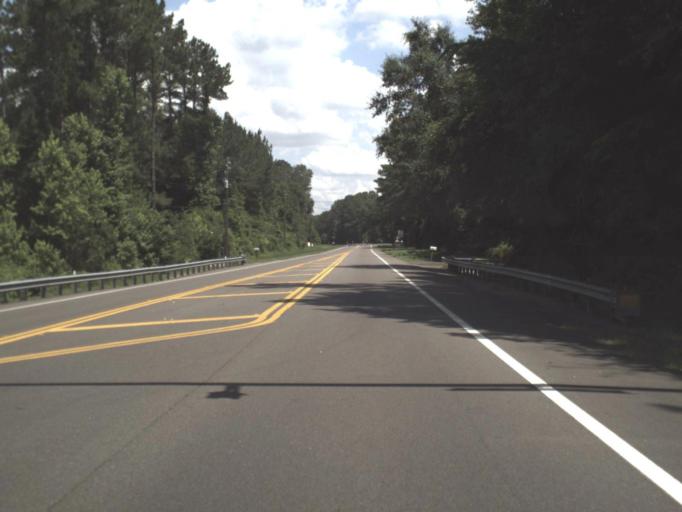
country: US
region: Florida
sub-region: Nassau County
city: Nassau Village-Ratliff
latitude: 30.5259
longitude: -81.7697
